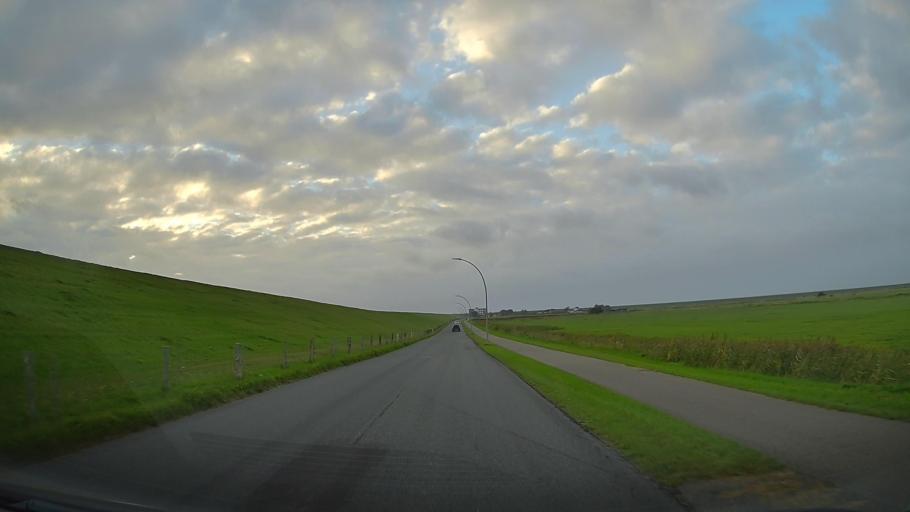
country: DE
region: Schleswig-Holstein
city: Husum
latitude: 54.4743
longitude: 9.0235
